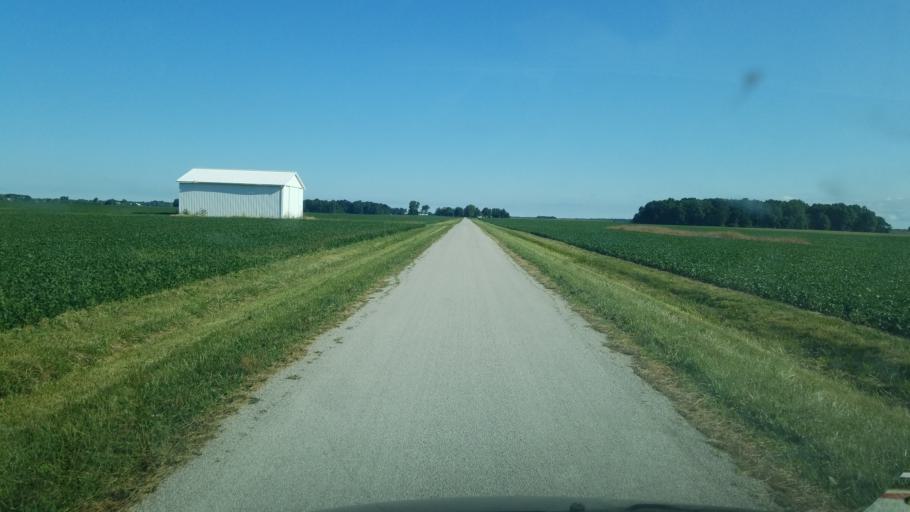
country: US
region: Ohio
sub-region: Wyandot County
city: Upper Sandusky
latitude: 40.8956
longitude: -83.2899
